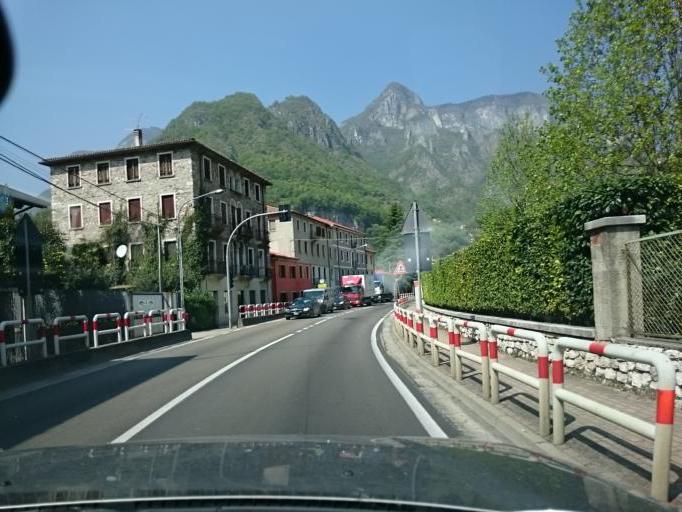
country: IT
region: Veneto
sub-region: Provincia di Vicenza
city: Valstagna
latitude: 45.8584
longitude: 11.6611
